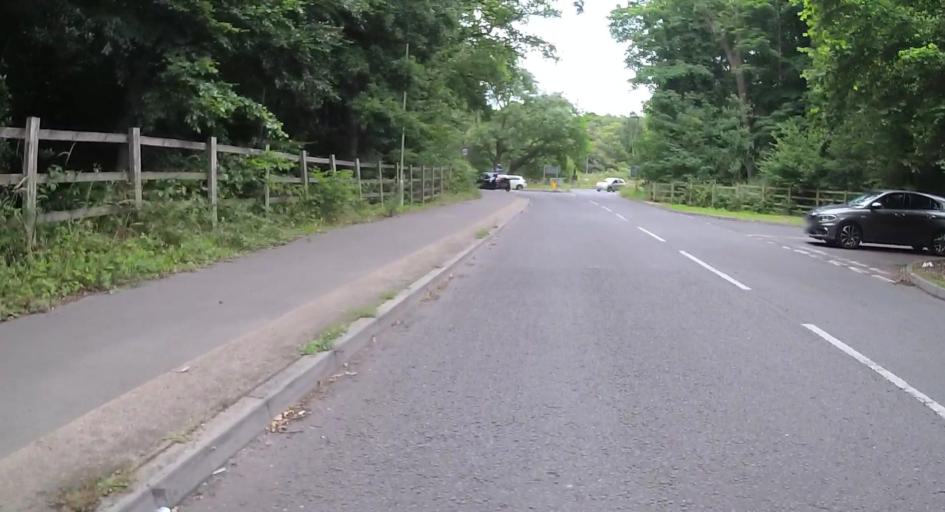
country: GB
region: England
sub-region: Hampshire
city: Fleet
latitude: 51.2535
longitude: -0.8257
